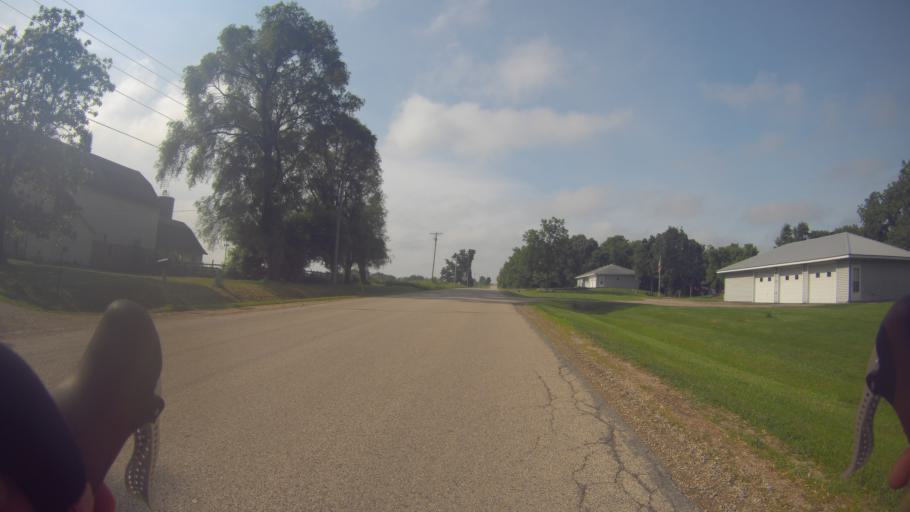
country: US
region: Wisconsin
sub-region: Dane County
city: McFarland
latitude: 43.0125
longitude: -89.2347
